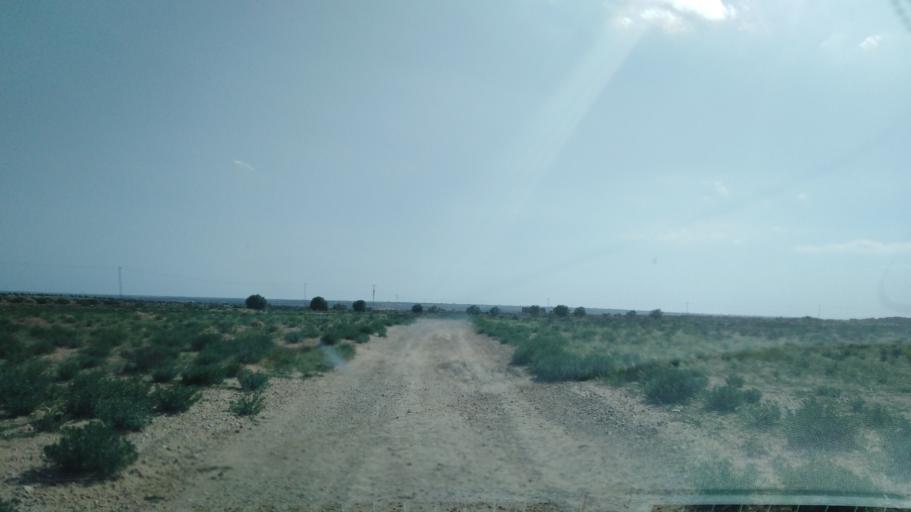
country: TN
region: Safaqis
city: Bi'r `Ali Bin Khalifah
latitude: 34.7974
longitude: 10.3746
